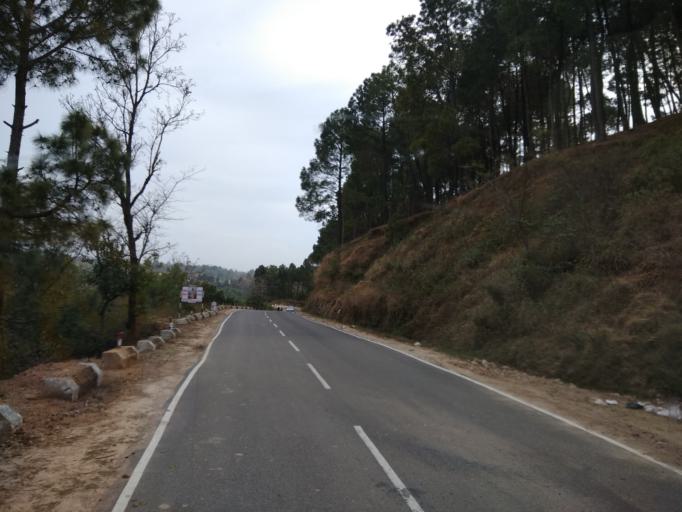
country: IN
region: Himachal Pradesh
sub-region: Kangra
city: Palampur
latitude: 32.1178
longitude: 76.4895
